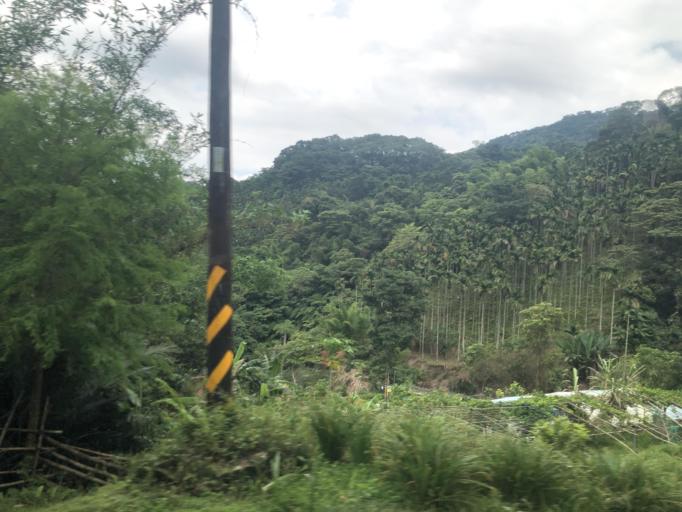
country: TW
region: Taipei
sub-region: Taipei
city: Banqiao
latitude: 24.8948
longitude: 121.4246
